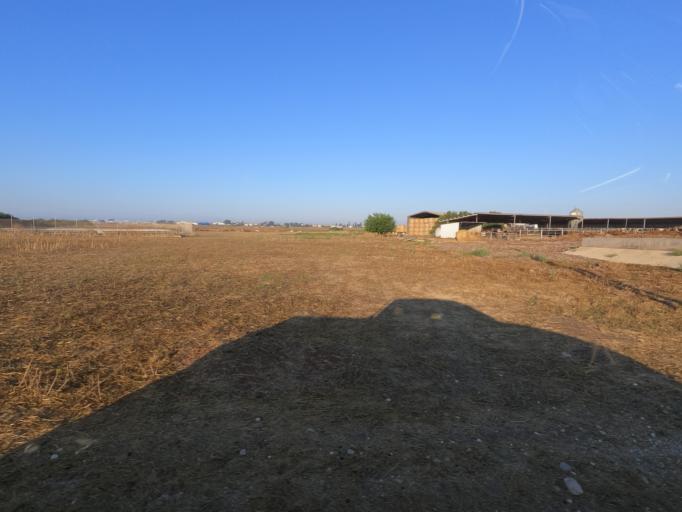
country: CY
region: Ammochostos
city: Achna
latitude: 35.0339
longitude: 33.7898
